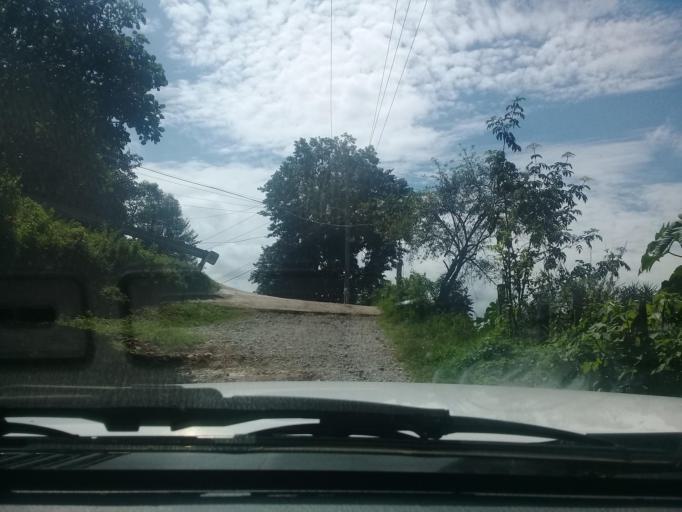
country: MX
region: Veracruz
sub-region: Tlalnelhuayocan
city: Otilpan
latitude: 19.5637
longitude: -96.9754
